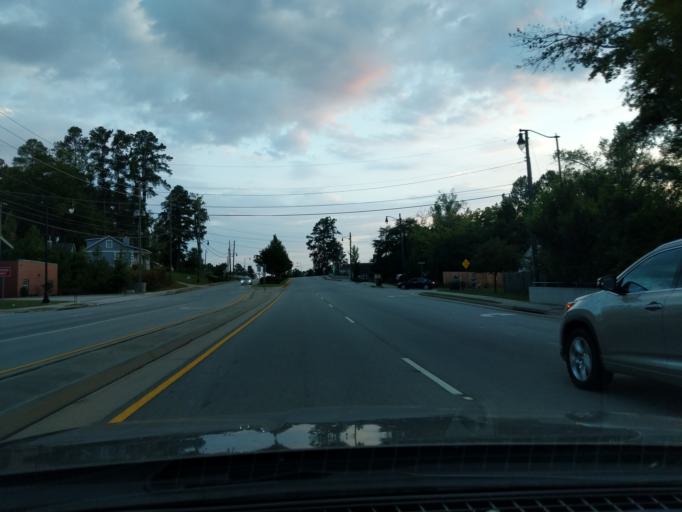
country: US
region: Georgia
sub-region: Columbia County
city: Martinez
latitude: 33.5145
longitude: -82.0262
